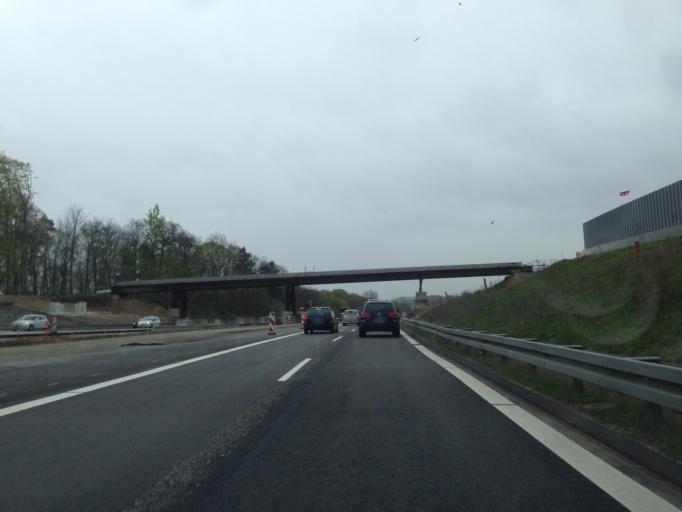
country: DK
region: Capital Region
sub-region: Rudersdal Kommune
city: Trorod
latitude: 55.8285
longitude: 12.5251
